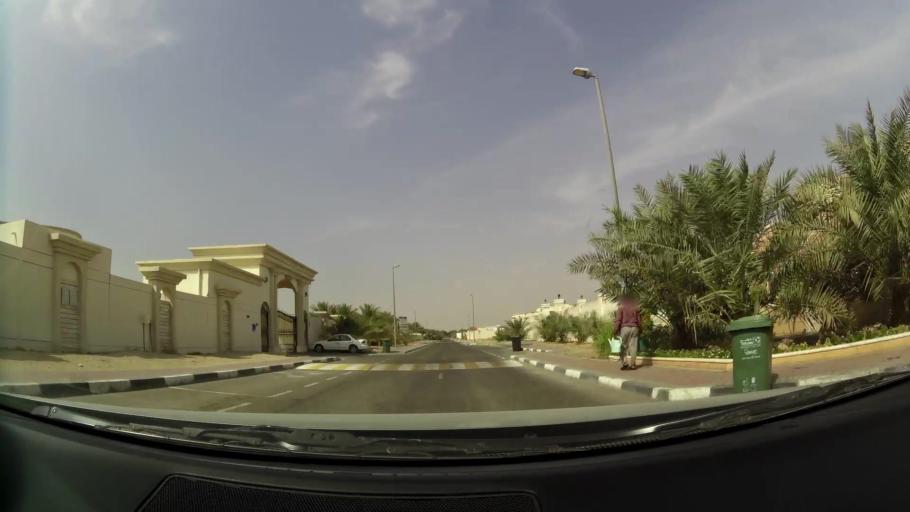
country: AE
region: Abu Dhabi
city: Al Ain
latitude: 24.1555
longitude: 55.6866
